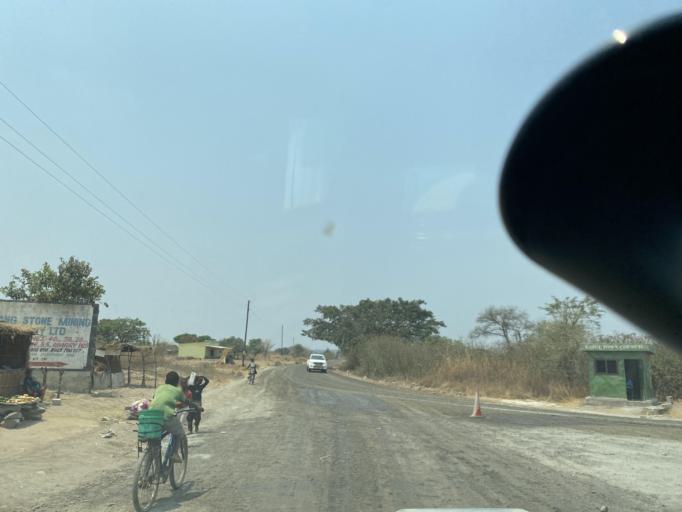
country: ZM
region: Lusaka
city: Lusaka
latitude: -15.5609
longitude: 28.4330
